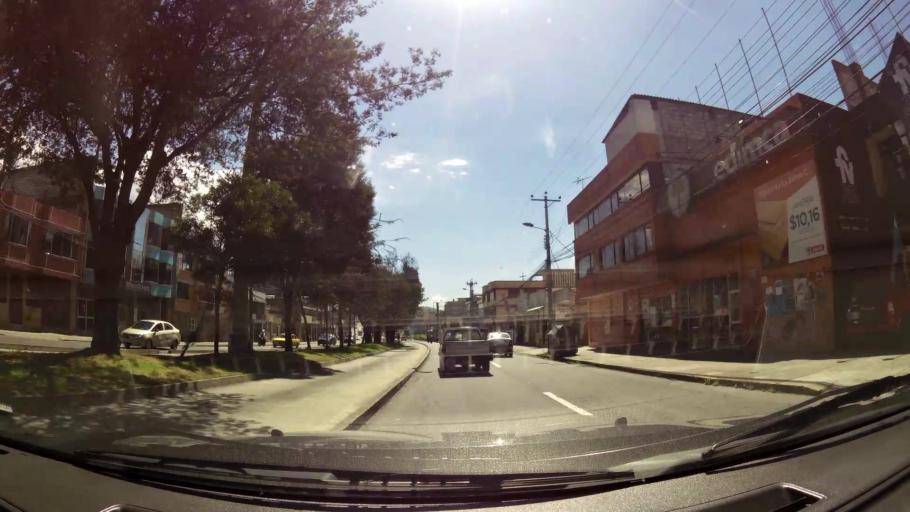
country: EC
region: Pichincha
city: Quito
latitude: -0.2553
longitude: -78.5414
